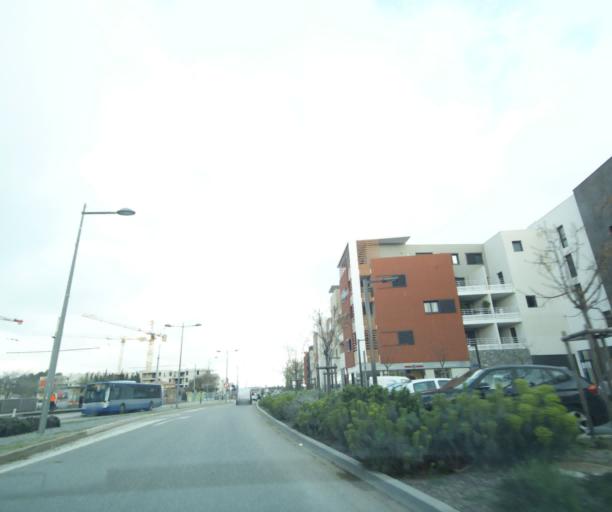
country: FR
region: Languedoc-Roussillon
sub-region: Departement de l'Herault
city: Saint-Jean-de-Vedas
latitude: 43.5750
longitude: 3.8299
